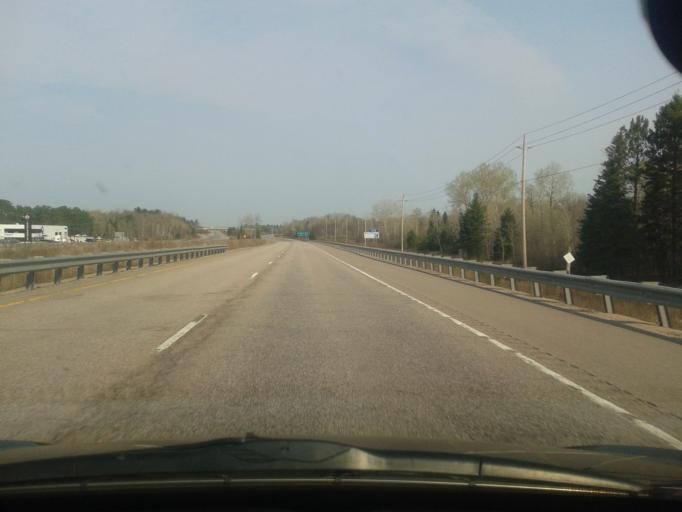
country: CA
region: Ontario
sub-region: Nipissing District
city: North Bay
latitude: 46.2585
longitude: -79.3821
